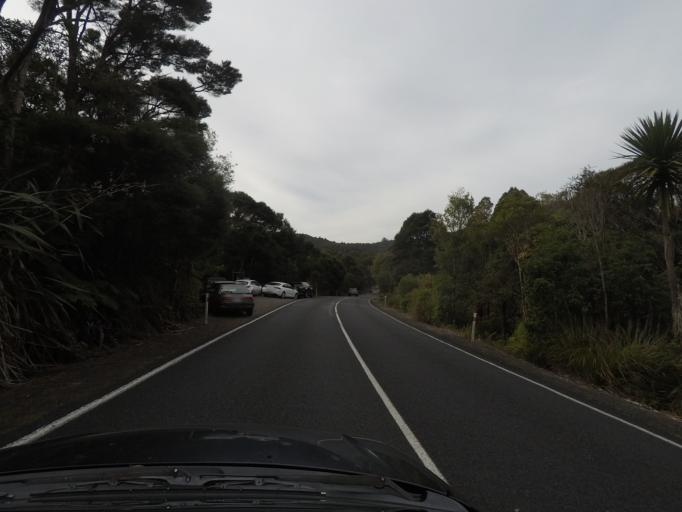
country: NZ
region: Auckland
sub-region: Auckland
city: Titirangi
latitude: -36.9369
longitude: 174.5563
